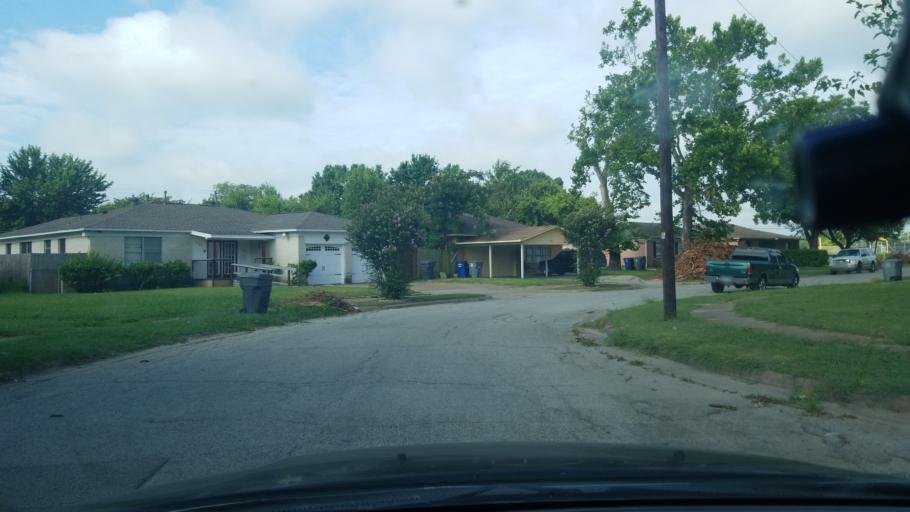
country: US
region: Texas
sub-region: Dallas County
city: Balch Springs
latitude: 32.7456
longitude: -96.6644
